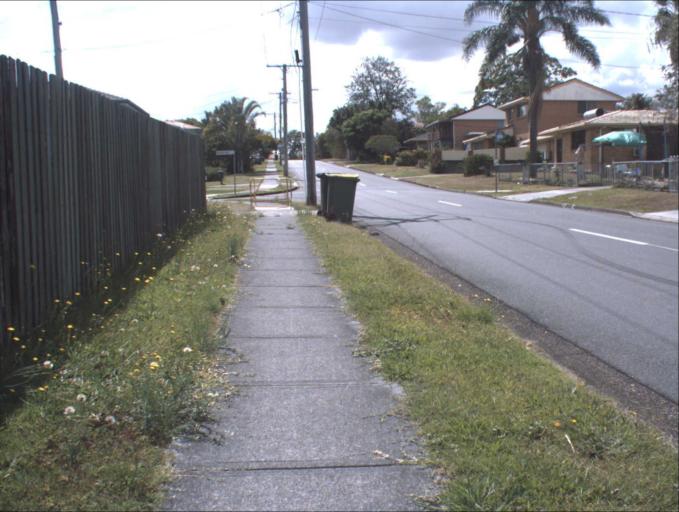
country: AU
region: Queensland
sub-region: Logan
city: Beenleigh
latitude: -27.7199
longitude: 153.1920
